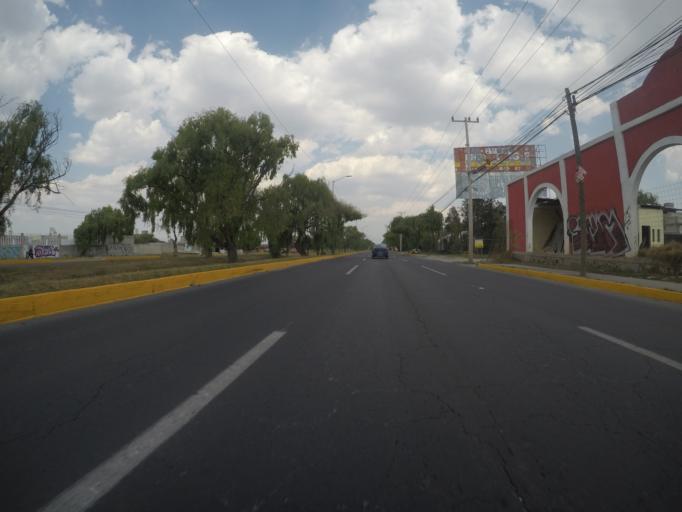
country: MX
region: Mexico
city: San Buenaventura
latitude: 19.2565
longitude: -99.6792
